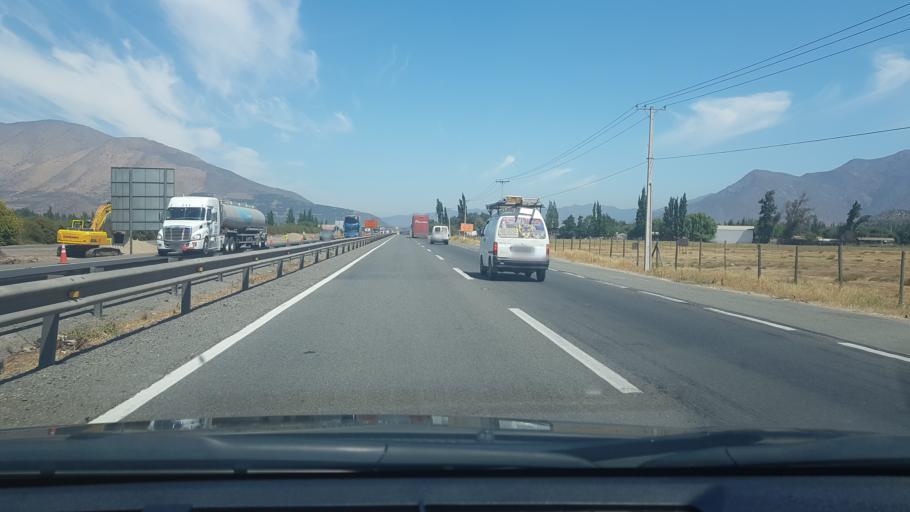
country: CL
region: Valparaiso
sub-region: Provincia de San Felipe
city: Llaillay
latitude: -32.8493
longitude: -70.9537
